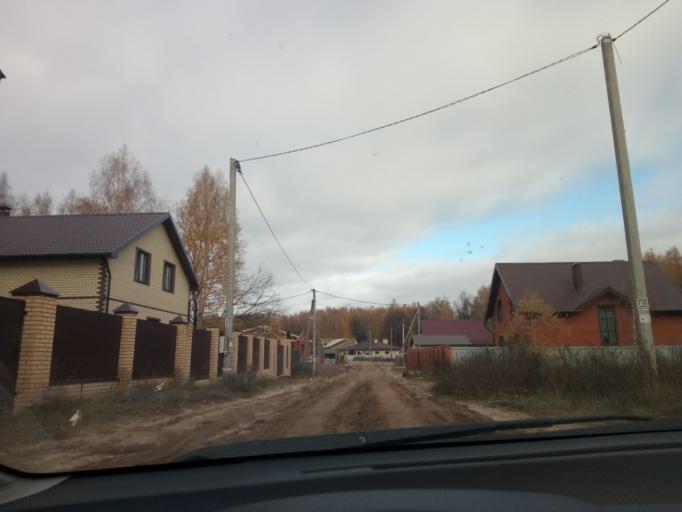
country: RU
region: Tatarstan
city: Staroye Arakchino
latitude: 55.9680
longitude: 49.0451
